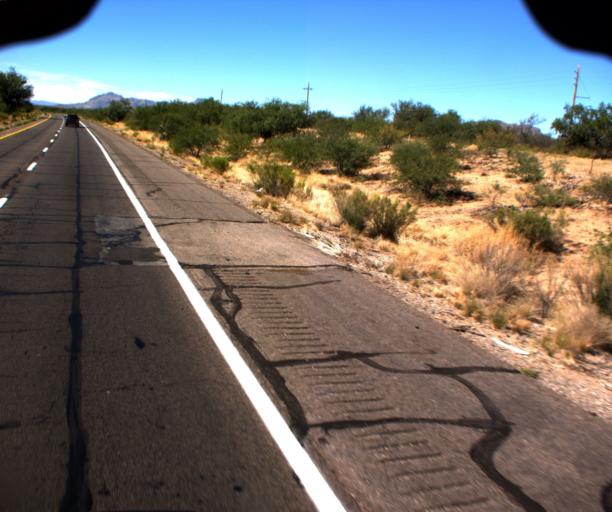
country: US
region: Arizona
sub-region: Pima County
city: Arivaca Junction
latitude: 31.7058
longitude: -111.0655
